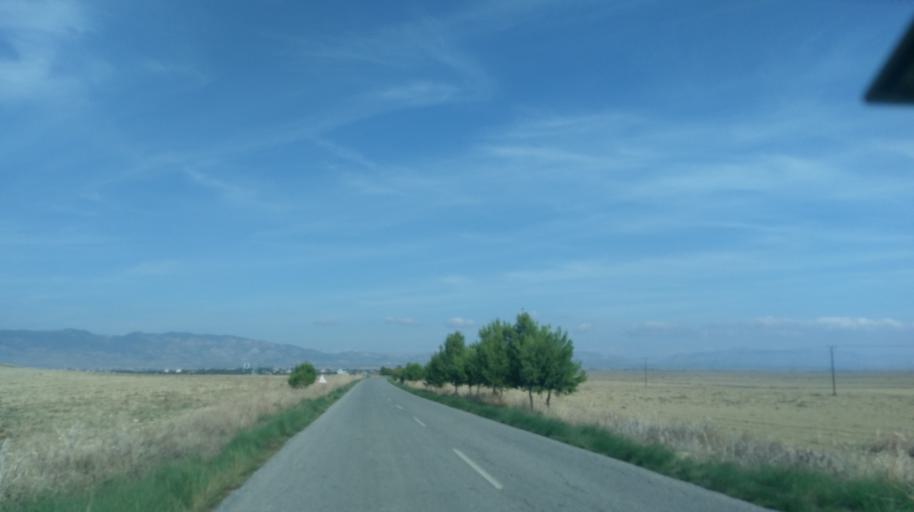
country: CY
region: Ammochostos
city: Lefkonoiko
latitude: 35.1967
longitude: 33.6189
